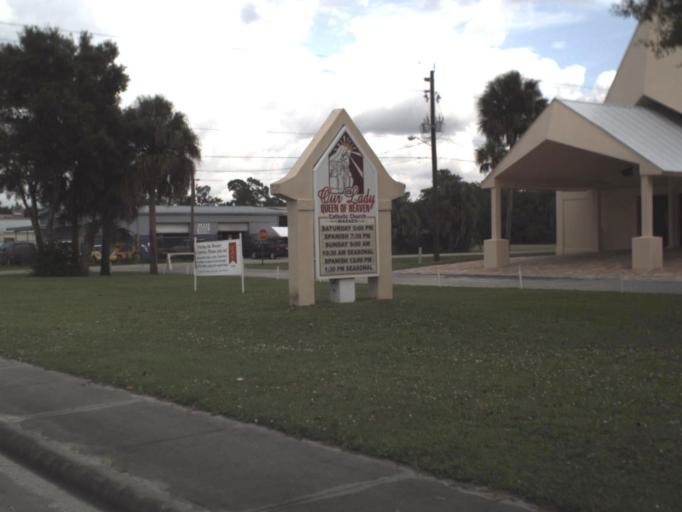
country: US
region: Florida
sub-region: Hendry County
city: LaBelle
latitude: 26.7561
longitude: -81.4373
